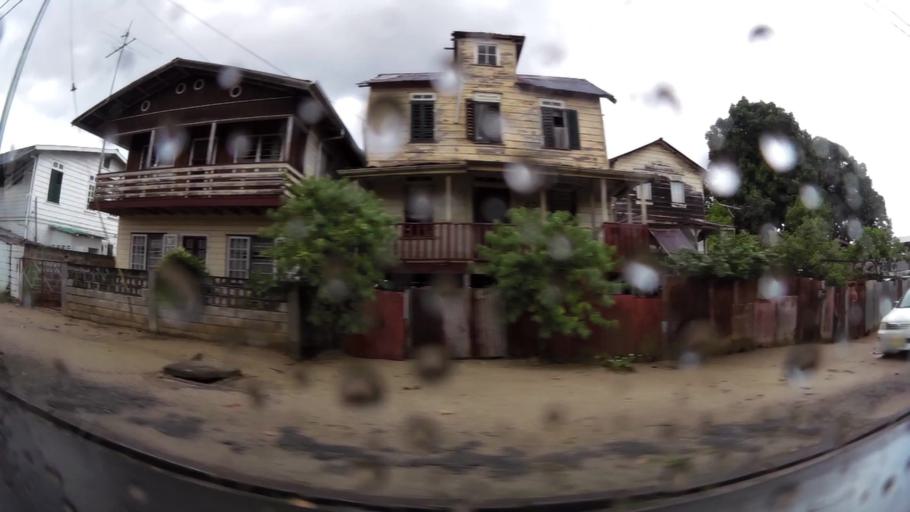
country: SR
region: Paramaribo
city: Paramaribo
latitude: 5.8335
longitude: -55.1660
